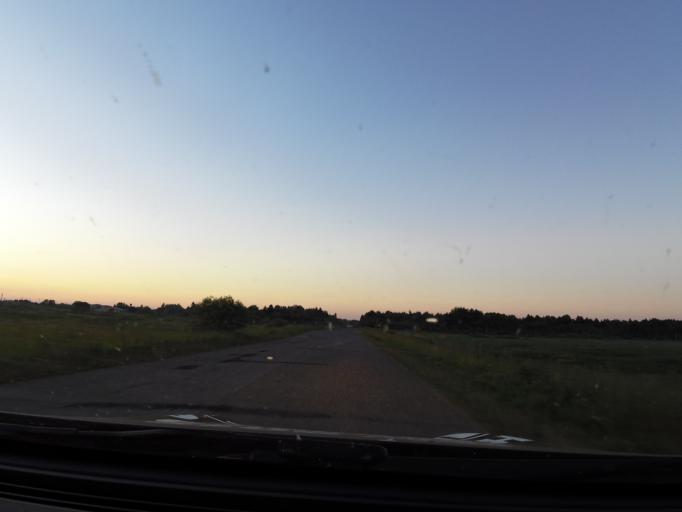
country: RU
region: Kostroma
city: Buy
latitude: 58.3815
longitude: 41.2161
